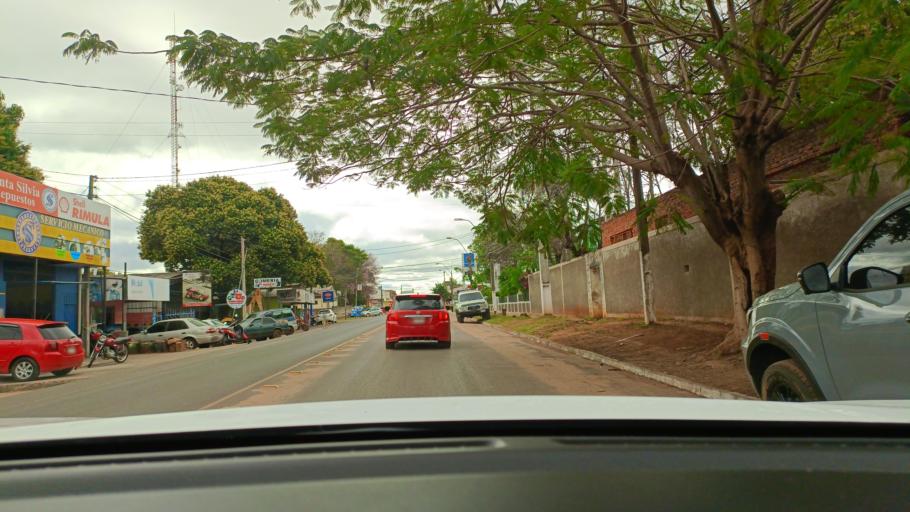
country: PY
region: San Pedro
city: Guayaybi
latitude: -24.6744
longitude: -56.4467
